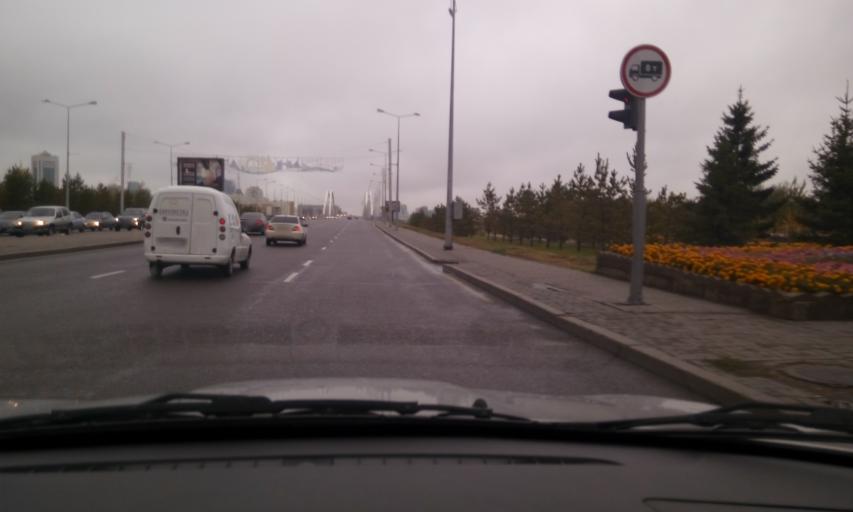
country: KZ
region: Astana Qalasy
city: Astana
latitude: 51.1296
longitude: 71.4581
